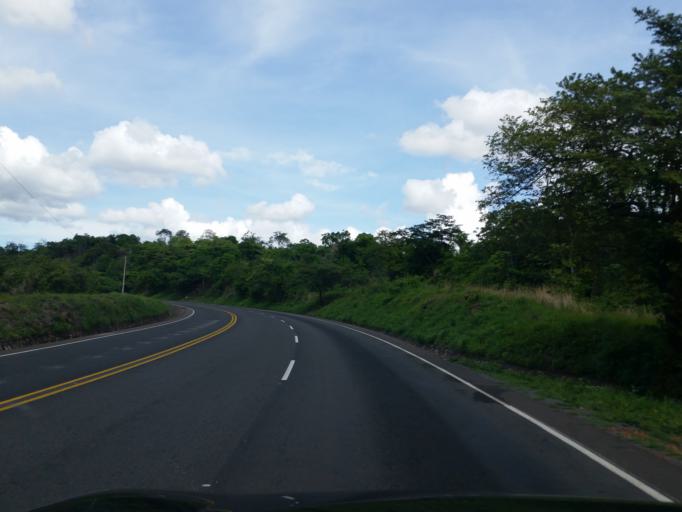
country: NI
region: Managua
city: Valle San Francisco
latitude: 12.4895
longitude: -86.0687
